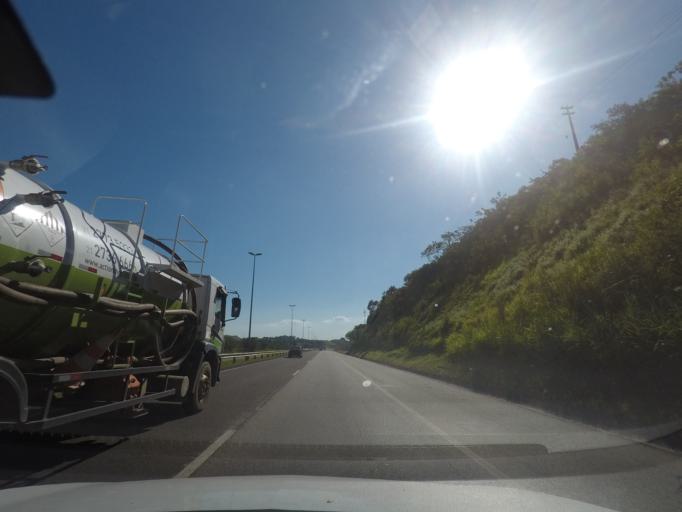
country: BR
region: Rio de Janeiro
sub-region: Guapimirim
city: Guapimirim
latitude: -22.6476
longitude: -43.0723
